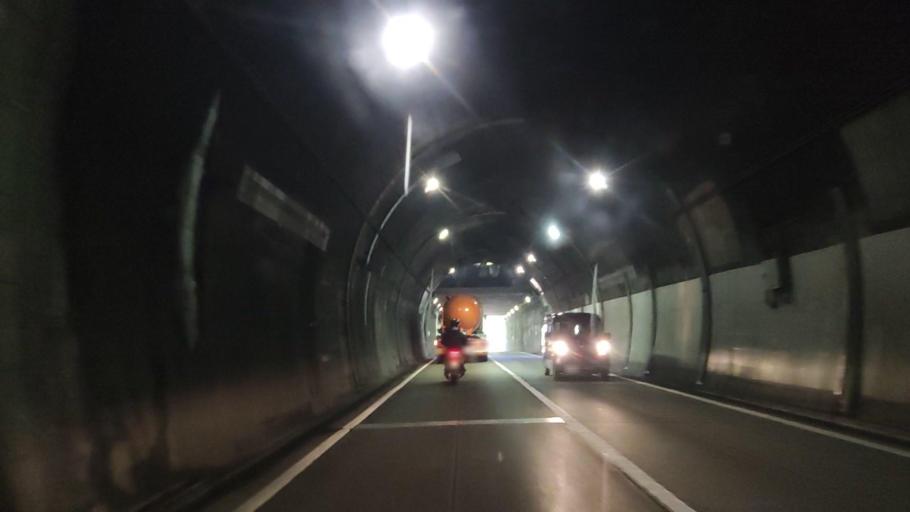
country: JP
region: Niigata
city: Itoigawa
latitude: 36.9917
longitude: 137.6960
